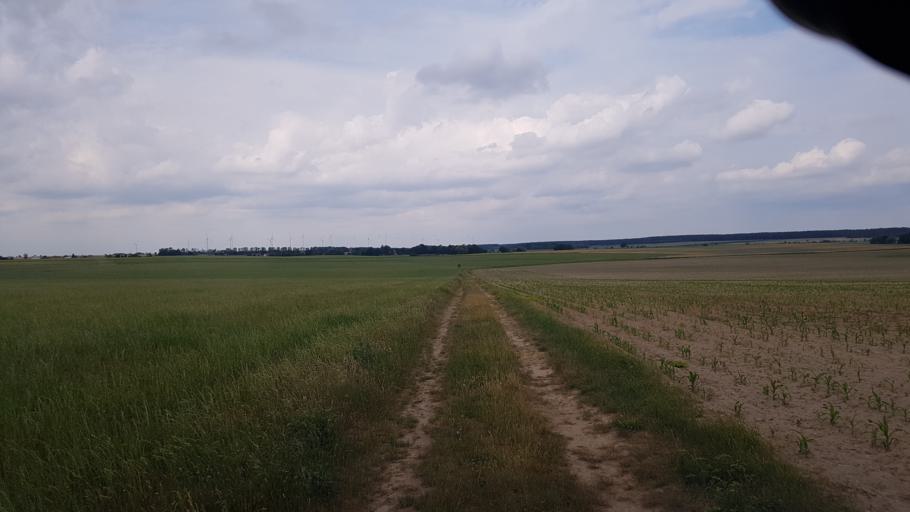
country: DE
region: Brandenburg
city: Dahme
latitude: 51.8806
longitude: 13.4021
